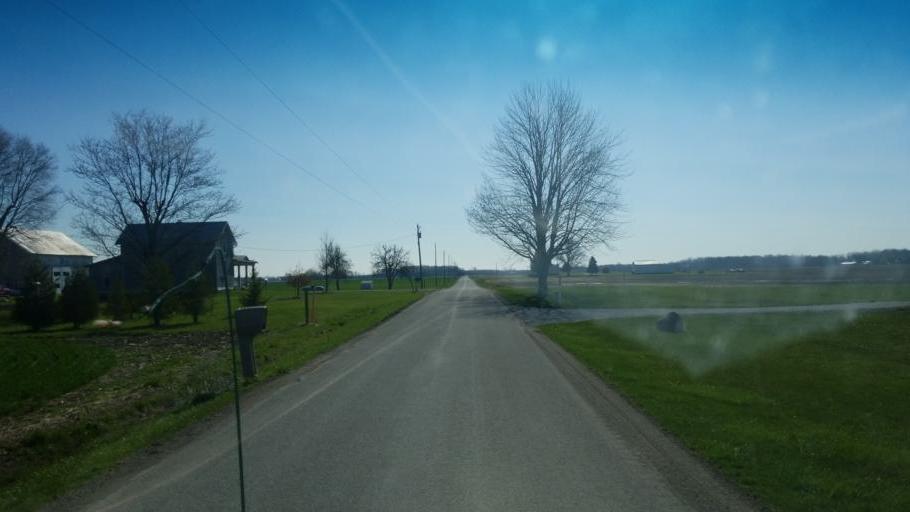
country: US
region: Ohio
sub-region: Hardin County
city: Forest
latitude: 40.7018
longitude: -83.5249
